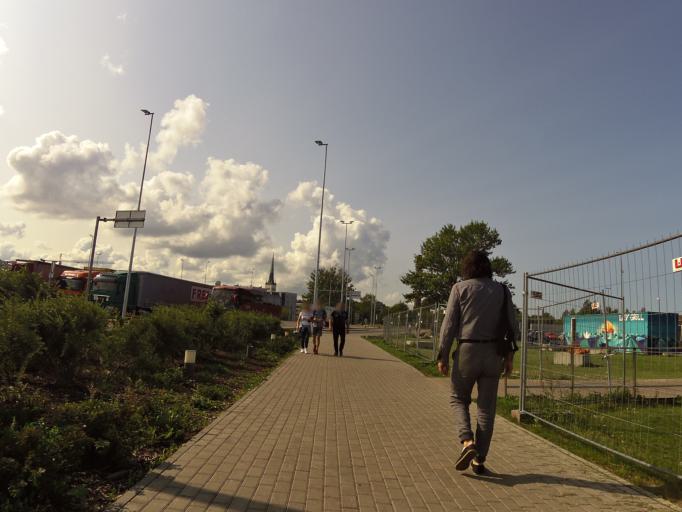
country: EE
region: Harju
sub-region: Tallinna linn
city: Tallinn
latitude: 59.4465
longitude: 24.7606
